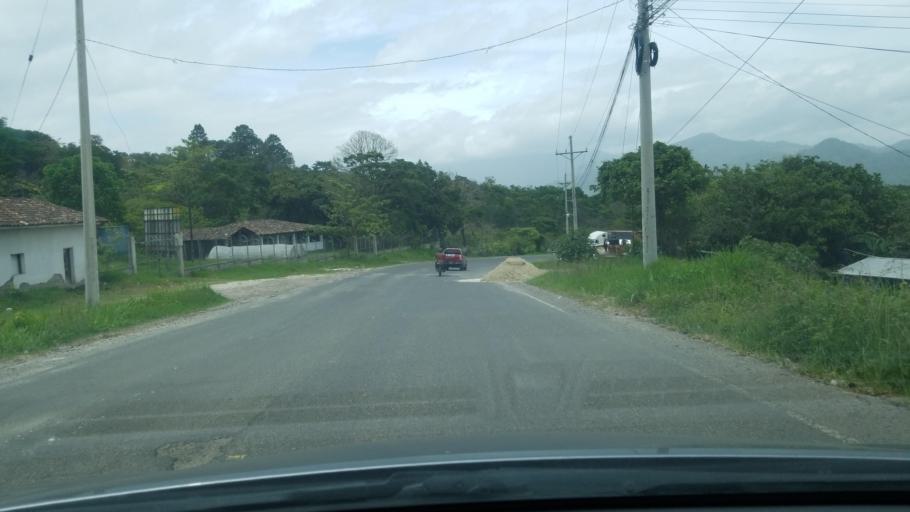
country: HN
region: Copan
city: Santa Rosa de Copan
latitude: 14.7489
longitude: -88.7713
